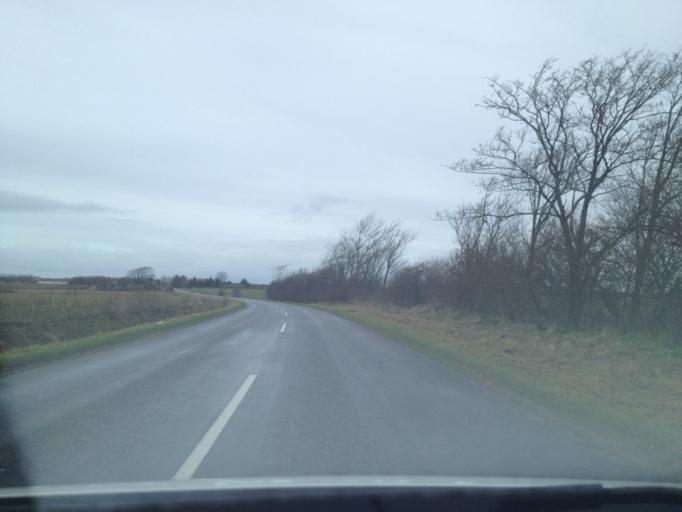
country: DK
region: South Denmark
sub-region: Tonder Kommune
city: Sherrebek
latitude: 55.2253
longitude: 8.8346
